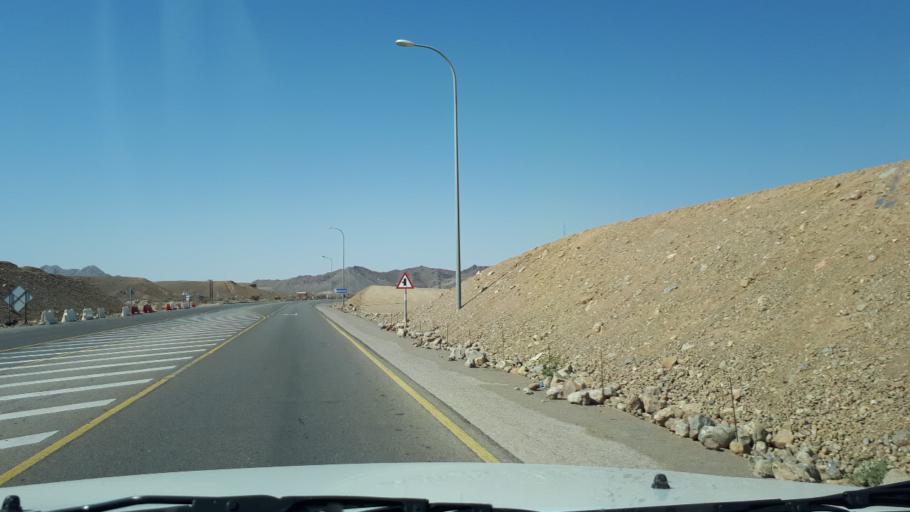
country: OM
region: Ash Sharqiyah
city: Sur
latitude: 22.3757
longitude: 59.3197
